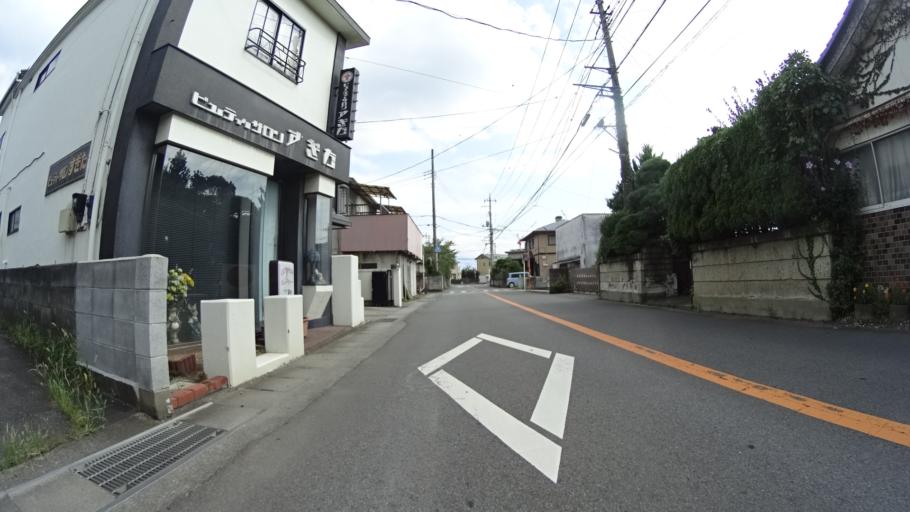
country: JP
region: Yamanashi
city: Kofu-shi
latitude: 35.6834
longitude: 138.5668
